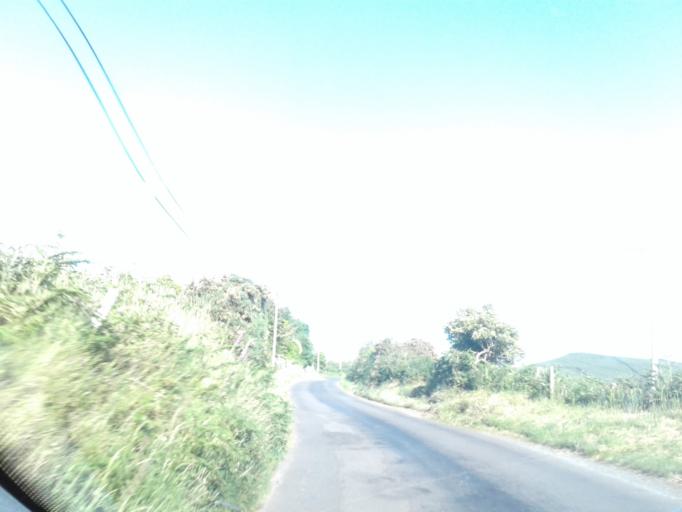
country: IE
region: Leinster
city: Ballinteer
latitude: 53.1902
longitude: -6.2575
